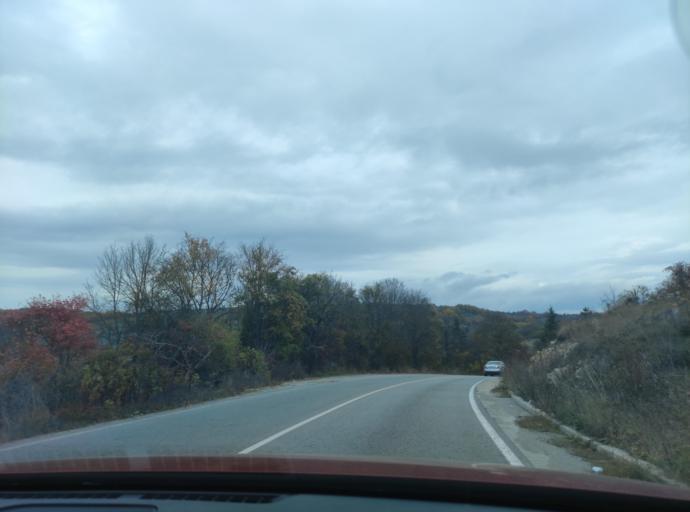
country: BG
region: Sofiya
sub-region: Obshtina Godech
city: Godech
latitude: 42.9625
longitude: 23.1548
